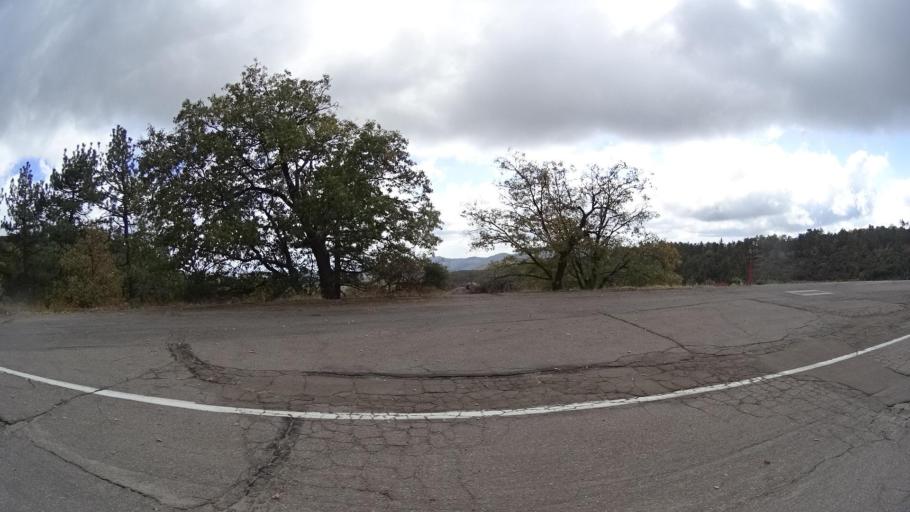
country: US
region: California
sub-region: San Diego County
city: Pine Valley
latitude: 32.8447
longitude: -116.4429
